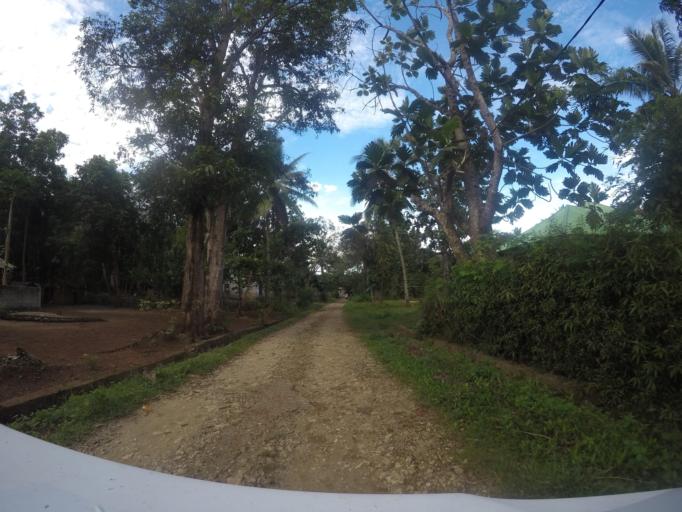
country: TL
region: Lautem
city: Lospalos
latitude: -8.5008
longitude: 126.9952
